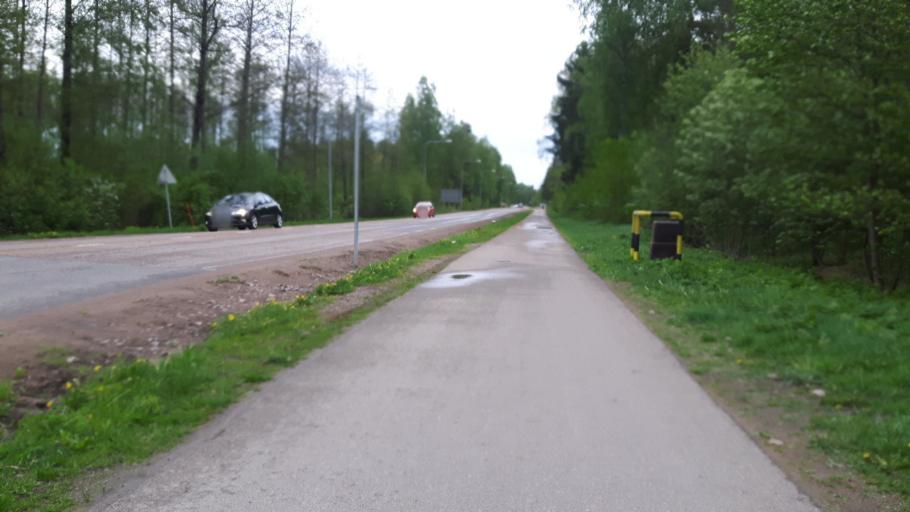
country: FI
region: Kymenlaakso
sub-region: Kotka-Hamina
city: Hamina
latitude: 60.5633
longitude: 27.1643
